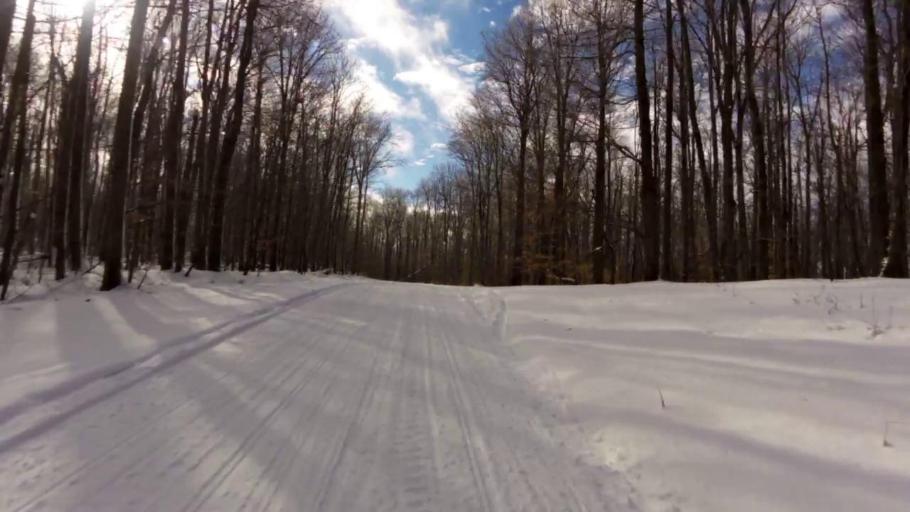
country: US
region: Pennsylvania
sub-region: McKean County
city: Bradford
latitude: 42.0331
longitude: -78.7110
